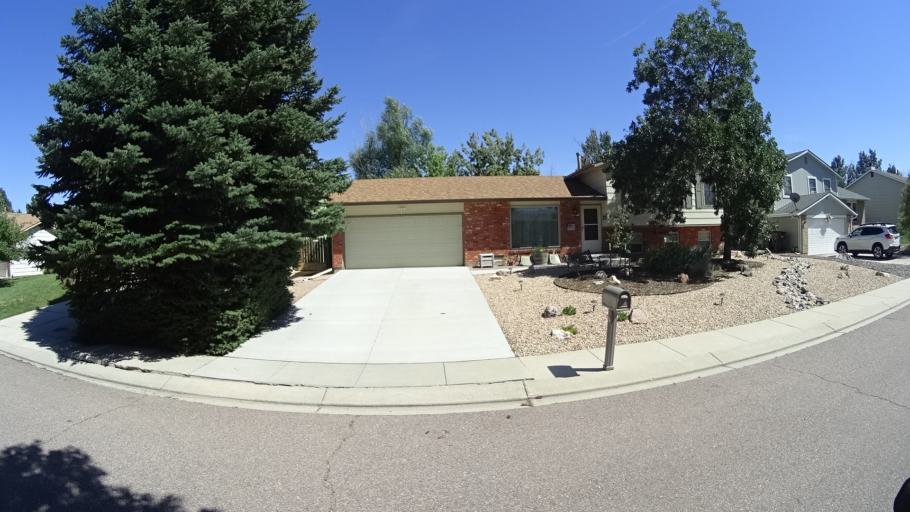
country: US
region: Colorado
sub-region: El Paso County
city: Colorado Springs
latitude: 38.9280
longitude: -104.7840
